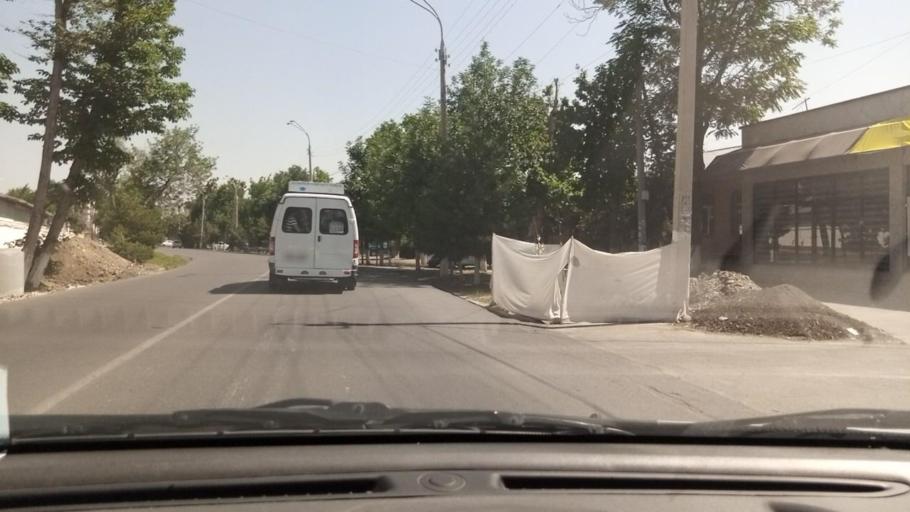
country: UZ
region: Toshkent Shahri
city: Tashkent
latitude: 41.2848
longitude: 69.2835
